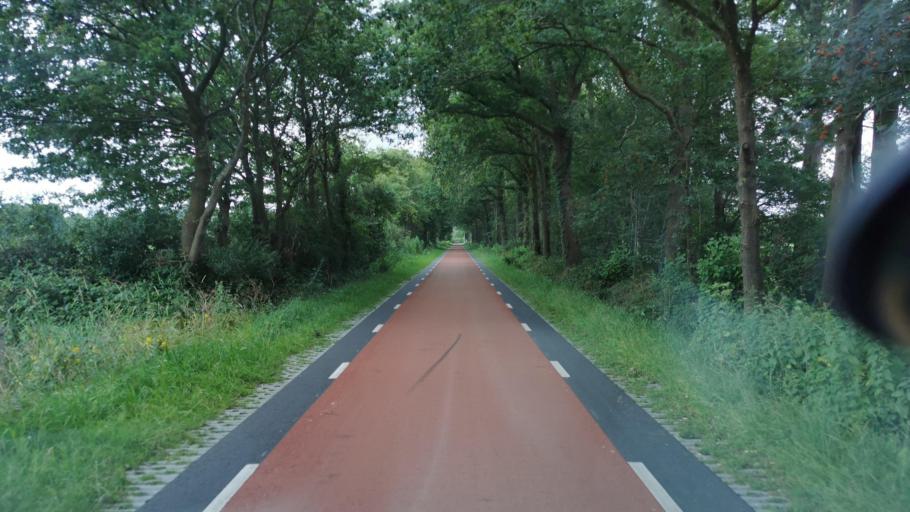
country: NL
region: Overijssel
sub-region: Gemeente Losser
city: Losser
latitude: 52.2572
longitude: 6.9922
